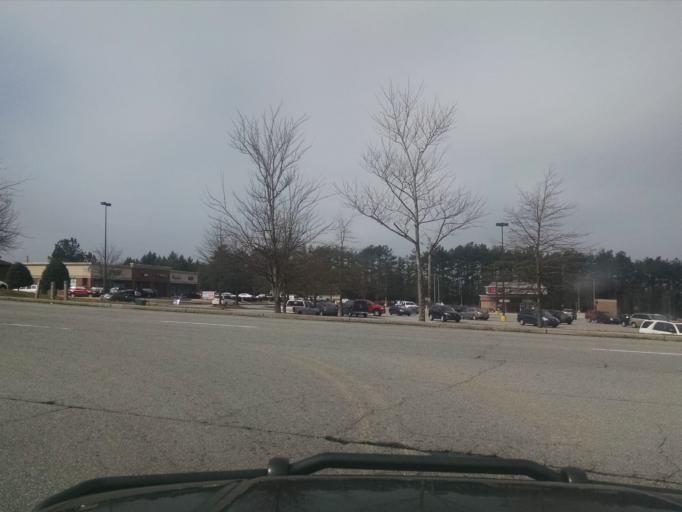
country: US
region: Georgia
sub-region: Gwinnett County
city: Buford
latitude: 34.0868
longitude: -83.9893
